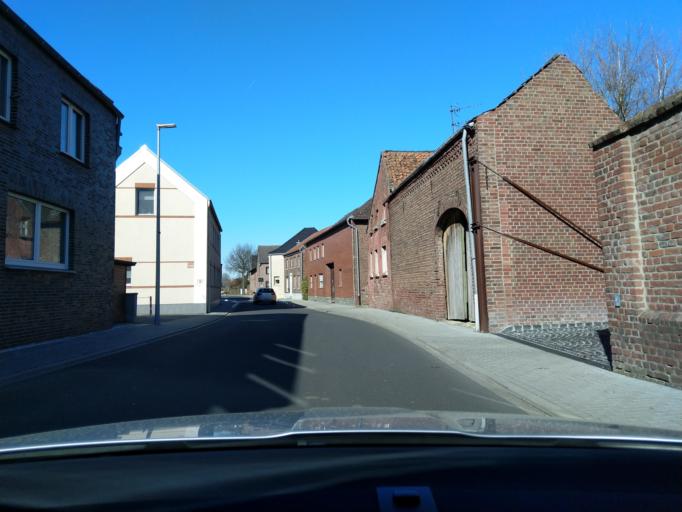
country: DE
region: North Rhine-Westphalia
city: Erkelenz
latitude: 51.1133
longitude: 6.3371
